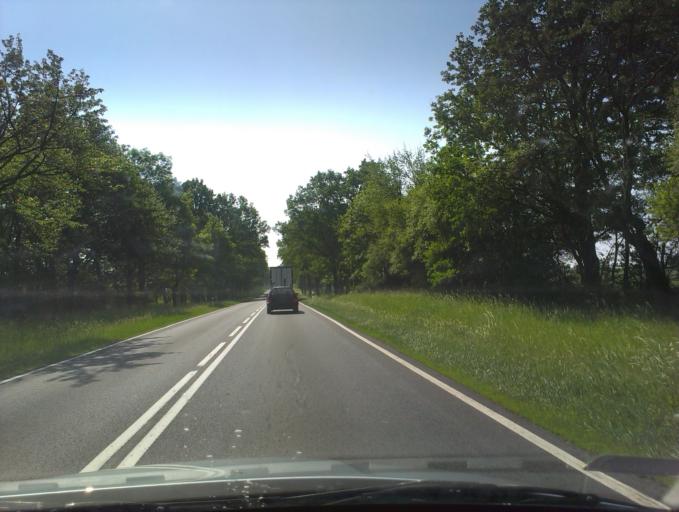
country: PL
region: Greater Poland Voivodeship
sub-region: Powiat zlotowski
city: Okonek
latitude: 53.6232
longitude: 16.7794
